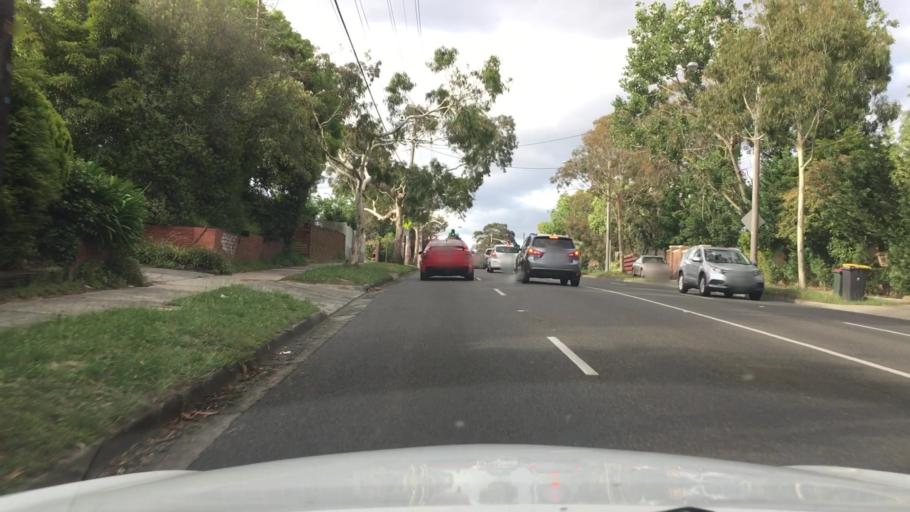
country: AU
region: Victoria
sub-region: Whitehorse
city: Burwood
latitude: -37.8667
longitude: 145.1306
